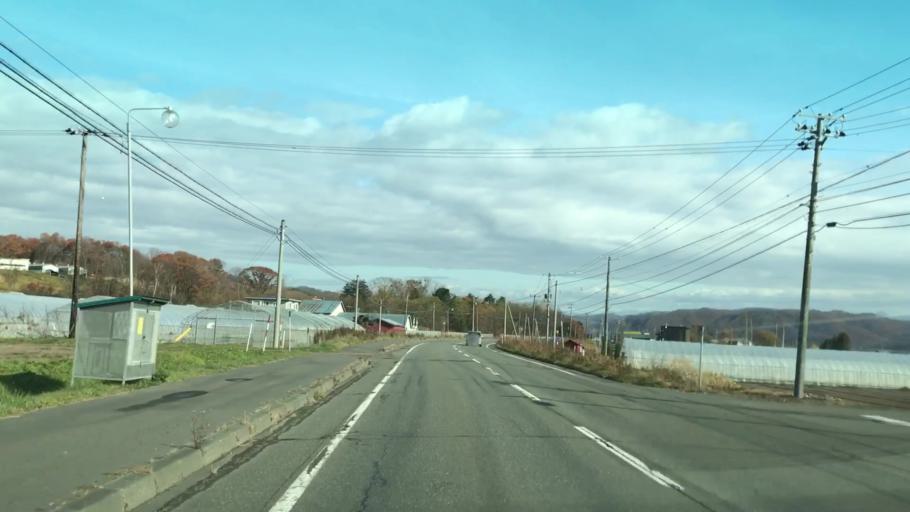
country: JP
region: Hokkaido
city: Shizunai-furukawacho
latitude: 42.5748
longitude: 142.1063
